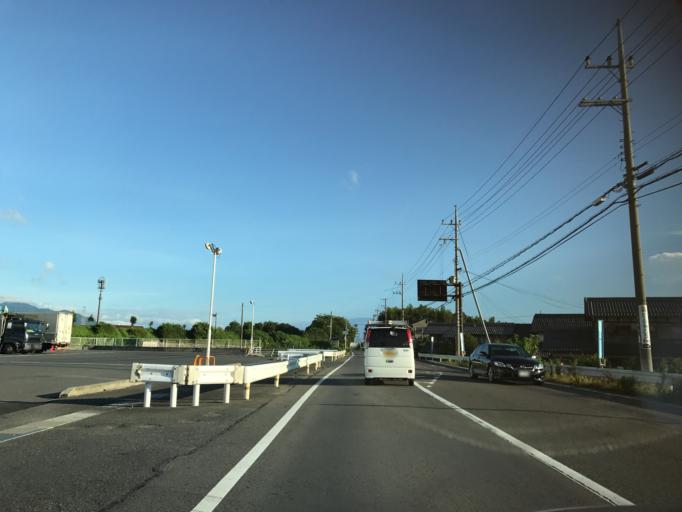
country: JP
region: Shiga Prefecture
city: Youkaichi
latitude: 35.1197
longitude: 136.2567
